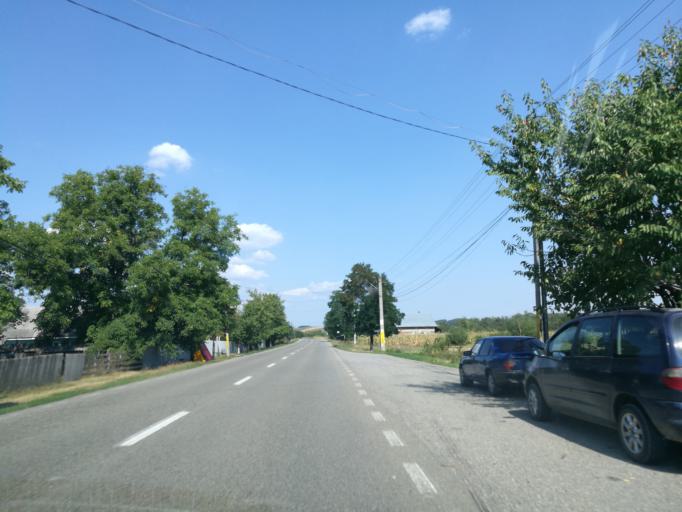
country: RO
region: Neamt
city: Bodesti
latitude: 47.0441
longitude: 26.4058
